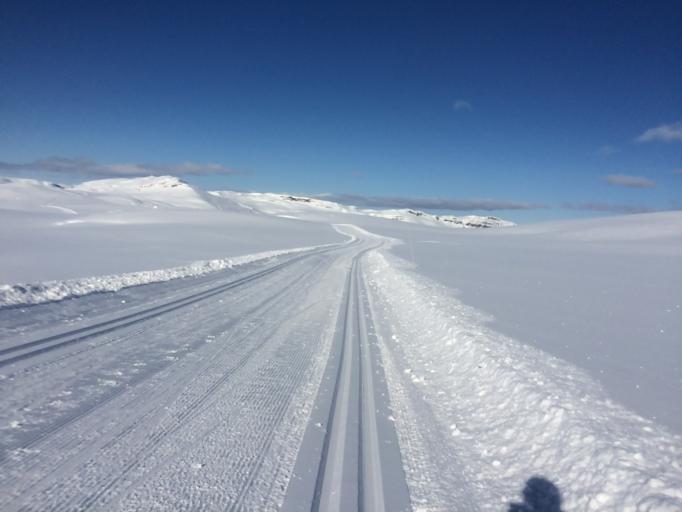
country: NO
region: Oppland
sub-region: Ringebu
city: Ringebu
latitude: 61.3542
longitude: 10.0868
